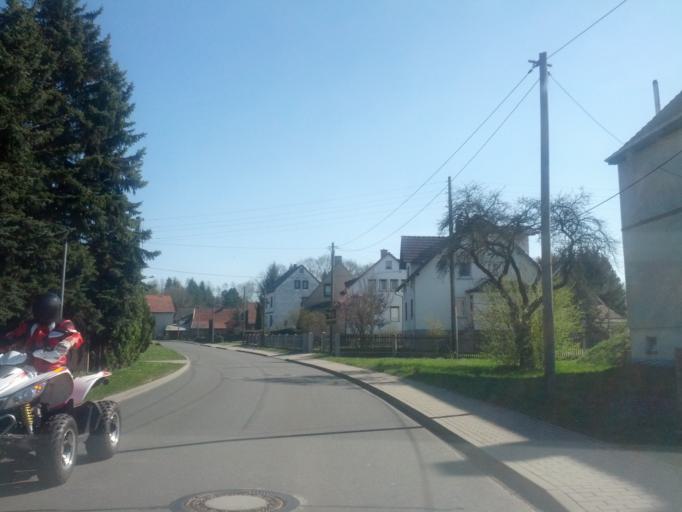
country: DE
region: Thuringia
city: Mechterstadt
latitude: 50.9296
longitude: 10.5400
